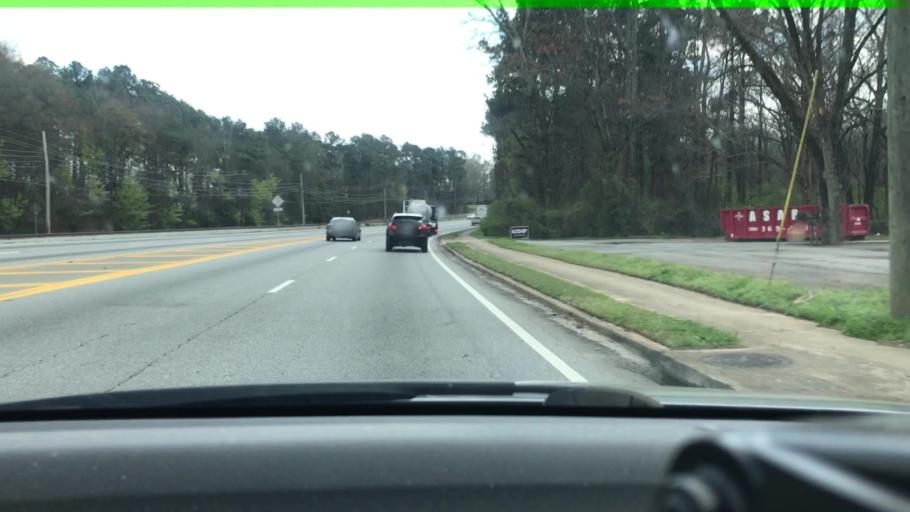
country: US
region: Georgia
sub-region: Clarke County
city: Country Club Estates
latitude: 33.9826
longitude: -83.4169
